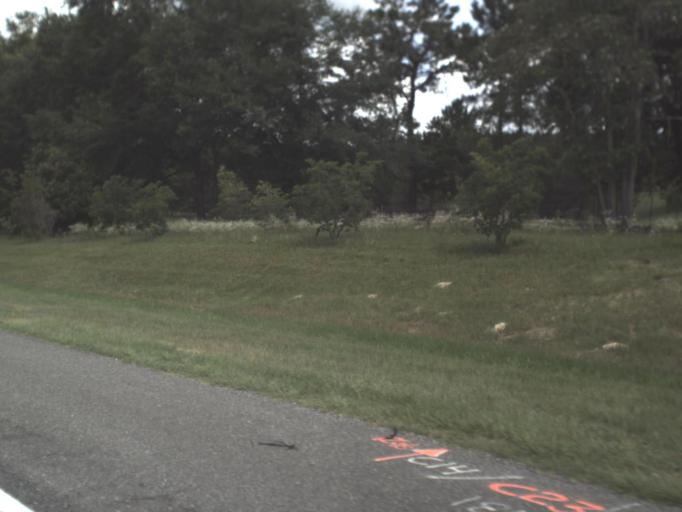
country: US
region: Florida
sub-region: Columbia County
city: Five Points
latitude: 30.2243
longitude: -82.7166
